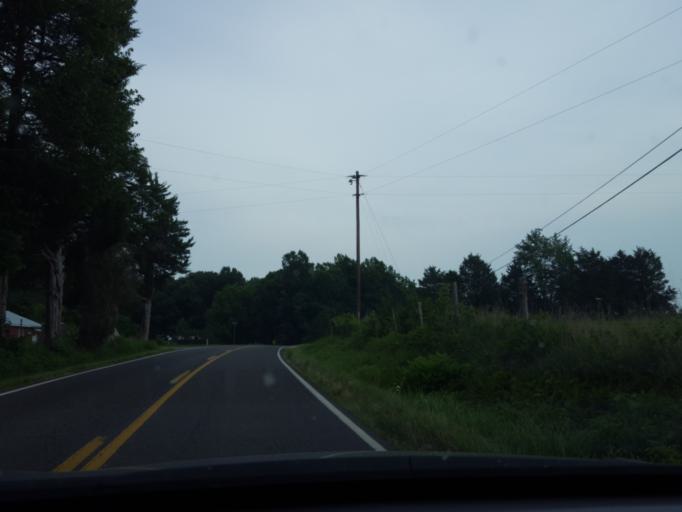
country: US
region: Virginia
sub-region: Orange County
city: Orange
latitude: 38.2601
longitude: -77.8603
